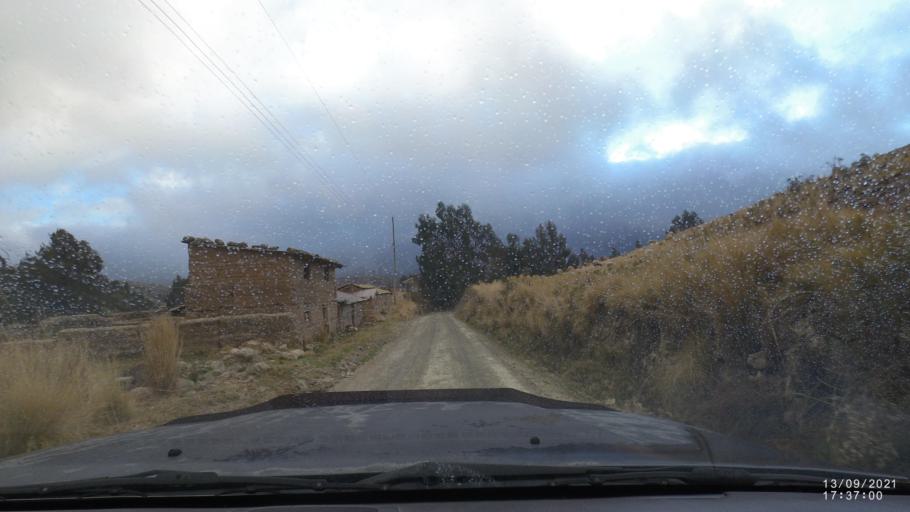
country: BO
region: Cochabamba
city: Colomi
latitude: -17.3617
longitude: -65.8030
